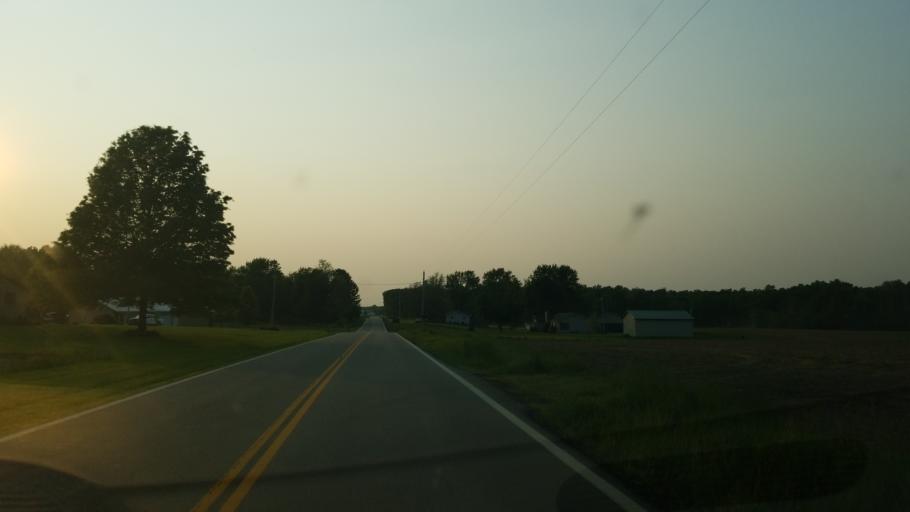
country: US
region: Ohio
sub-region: Ashland County
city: Ashland
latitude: 40.9464
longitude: -82.3268
